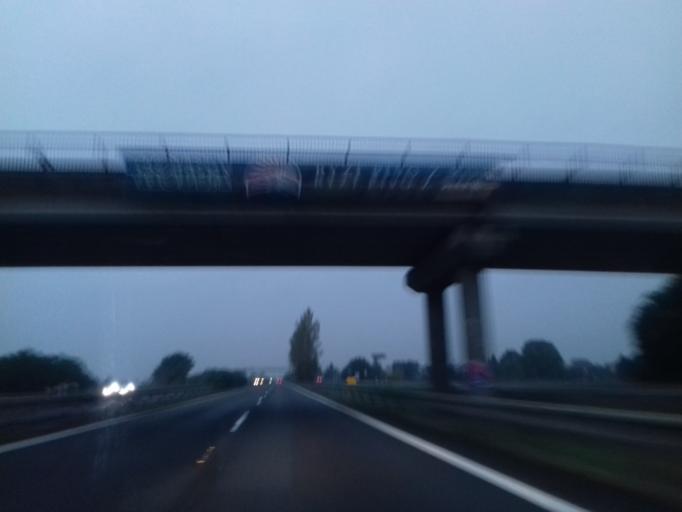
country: CZ
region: Olomoucky
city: Naklo
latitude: 49.6486
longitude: 17.1276
